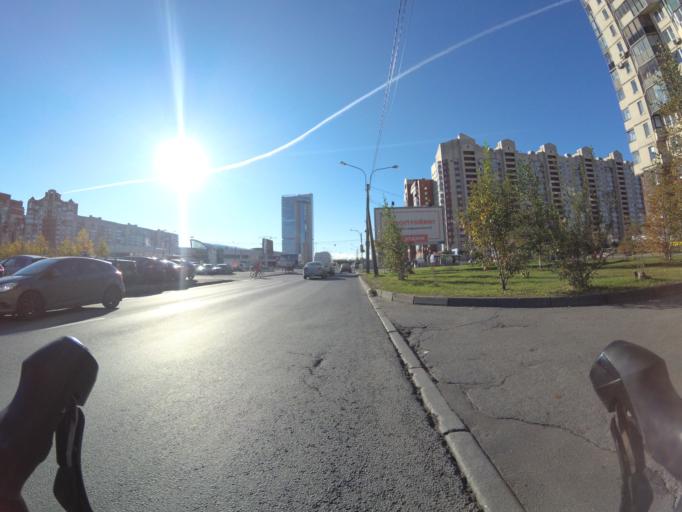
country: RU
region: Leningrad
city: Untolovo
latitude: 59.9895
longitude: 30.2032
